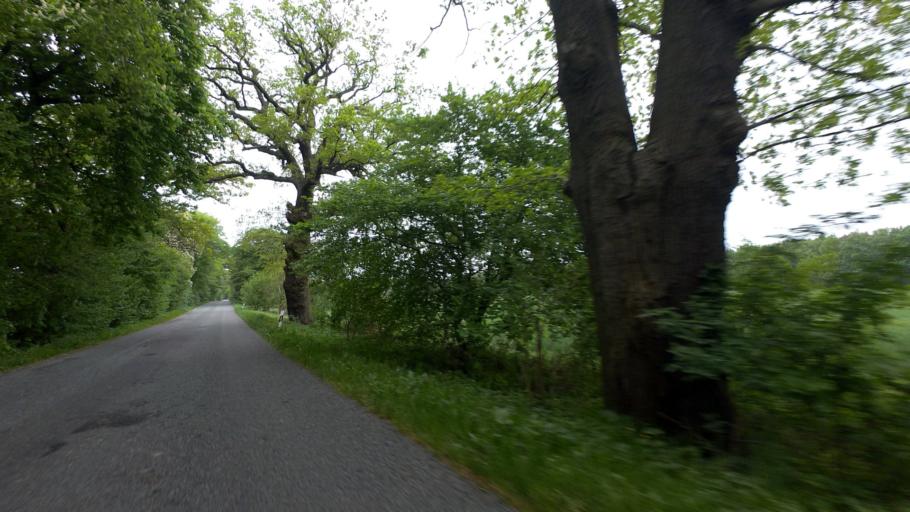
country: DE
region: Mecklenburg-Vorpommern
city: Mollenhagen
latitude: 53.6123
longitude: 12.9143
